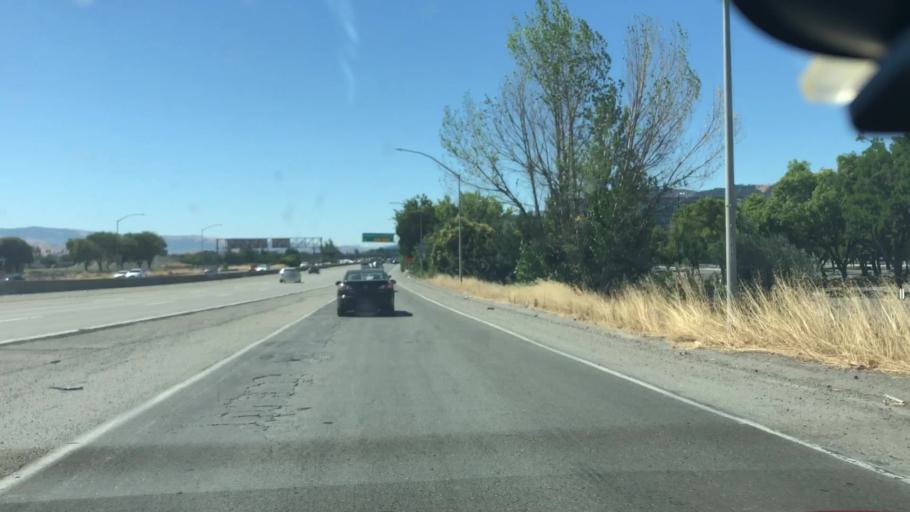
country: US
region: California
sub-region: Alameda County
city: Dublin
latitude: 37.6983
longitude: -121.9219
